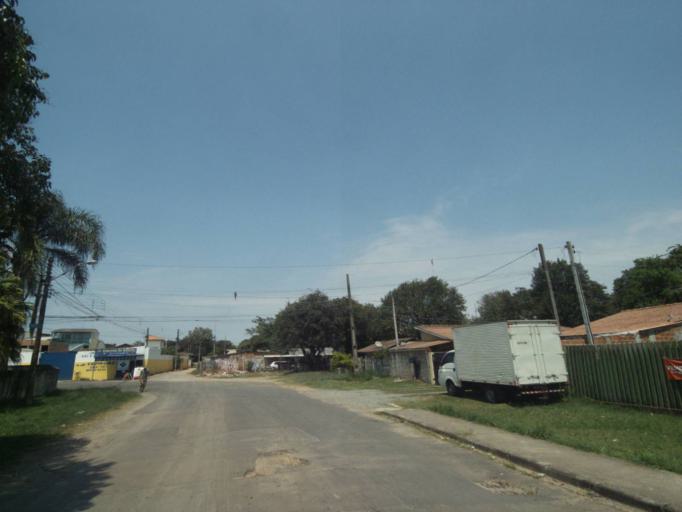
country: BR
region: Parana
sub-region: Curitiba
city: Curitiba
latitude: -25.4822
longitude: -49.3128
